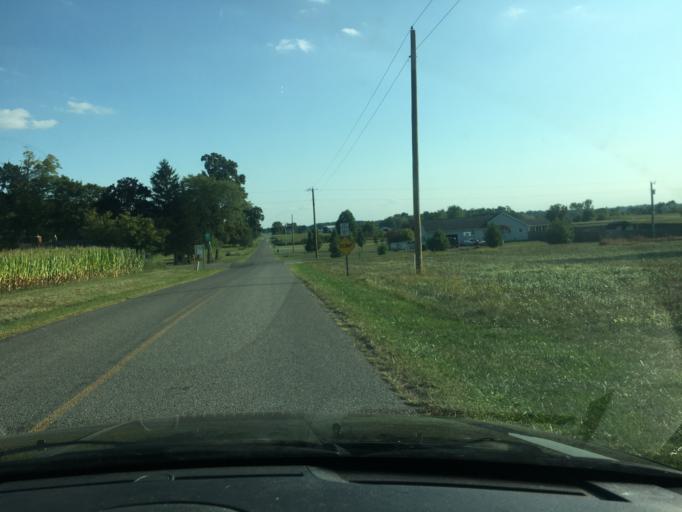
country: US
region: Ohio
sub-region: Logan County
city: West Liberty
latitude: 40.2617
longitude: -83.8030
